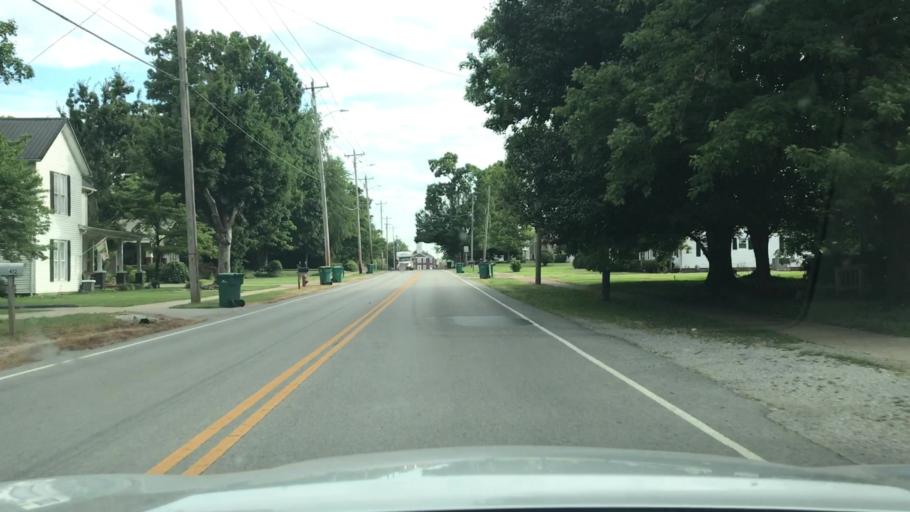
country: US
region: Kentucky
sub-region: Todd County
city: Elkton
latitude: 36.8046
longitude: -87.1555
